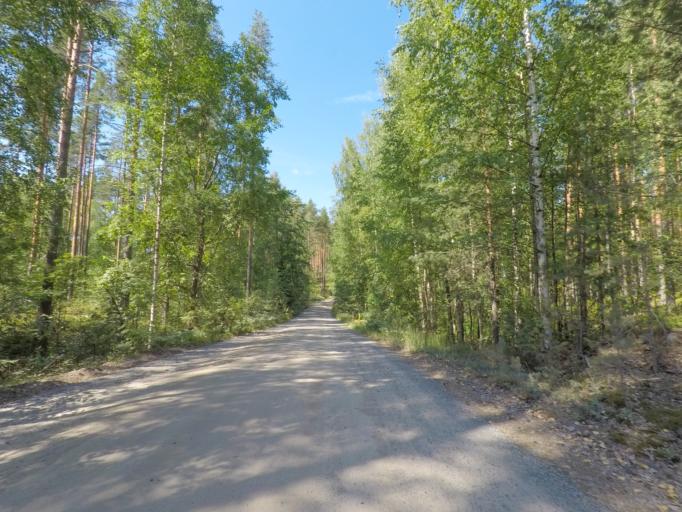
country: FI
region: Southern Savonia
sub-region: Mikkeli
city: Puumala
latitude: 61.4225
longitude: 28.0407
